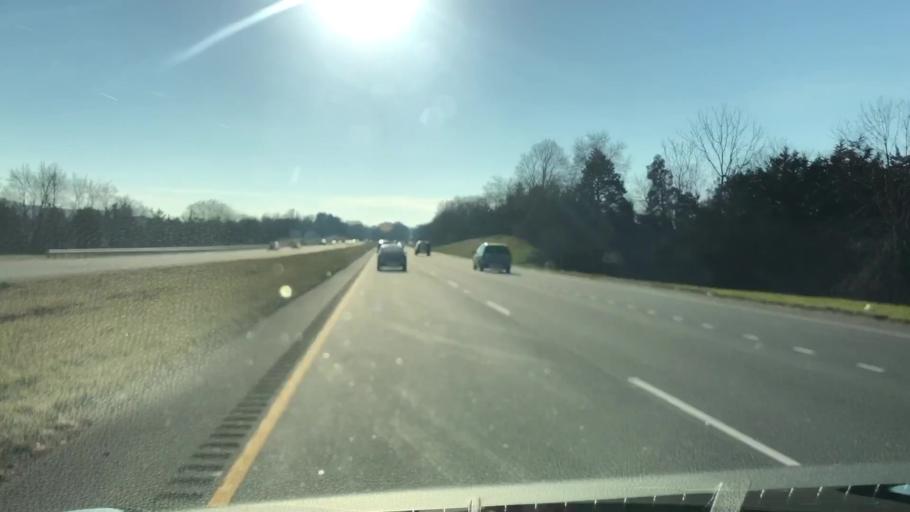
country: US
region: Virginia
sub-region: Culpeper County
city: Culpeper
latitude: 38.4710
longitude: -77.9556
